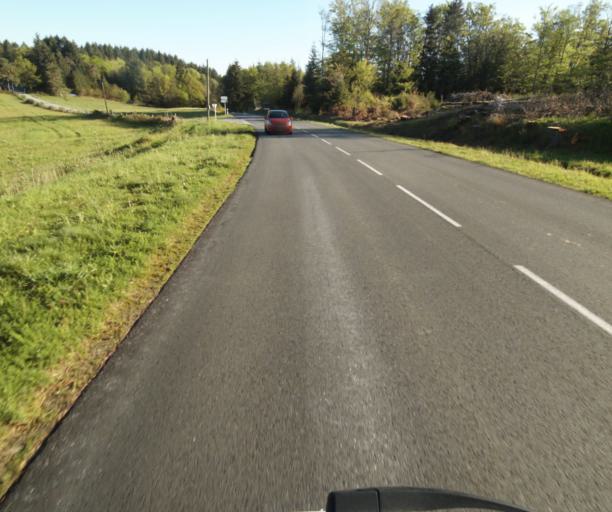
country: FR
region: Limousin
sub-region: Departement de la Correze
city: Correze
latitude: 45.3466
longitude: 1.8757
